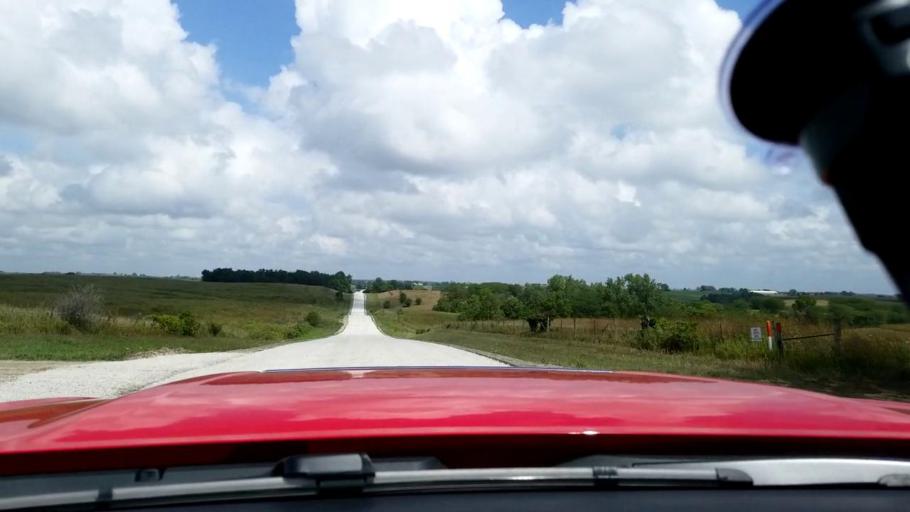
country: US
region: Iowa
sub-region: Decatur County
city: Lamoni
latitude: 40.6384
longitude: -94.0530
